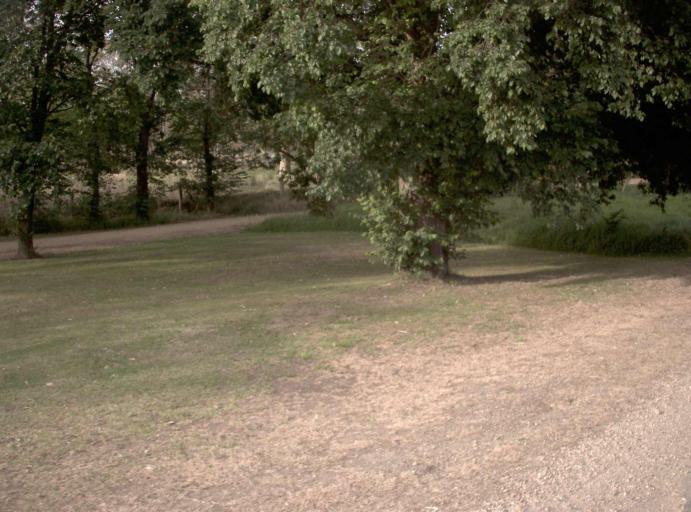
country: AU
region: Victoria
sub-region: Wellington
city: Heyfield
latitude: -37.9663
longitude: 146.9618
